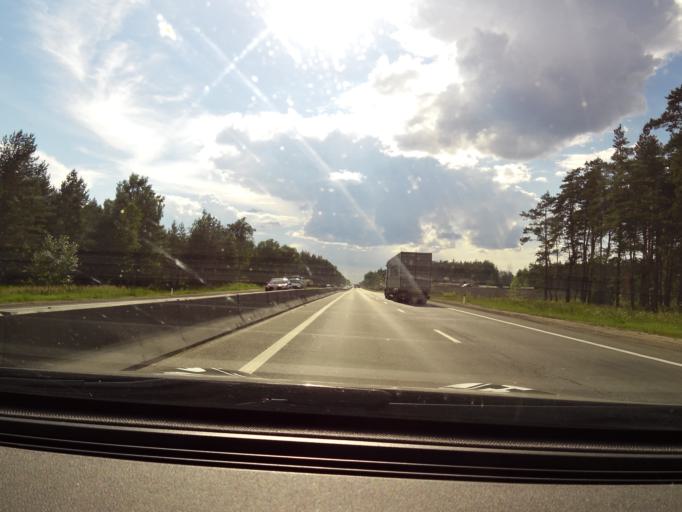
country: RU
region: Nizjnij Novgorod
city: Pyra
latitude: 56.2946
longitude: 43.3854
